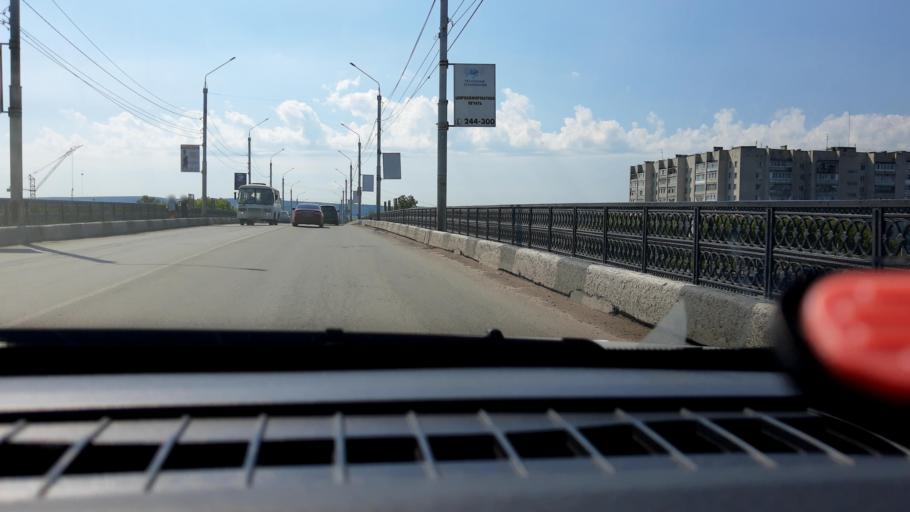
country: RU
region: Nizjnij Novgorod
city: Dzerzhinsk
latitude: 56.2355
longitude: 43.4884
